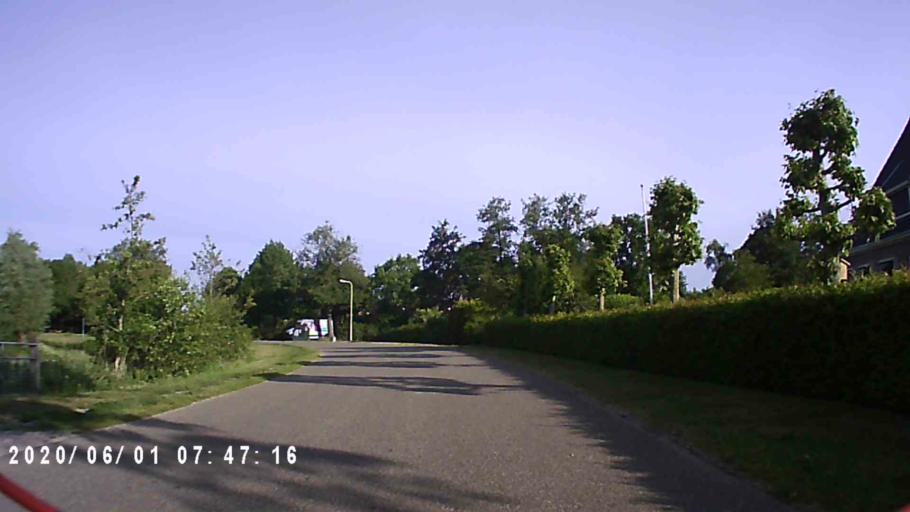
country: NL
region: Friesland
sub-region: Gemeente Dantumadiel
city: Rinsumageast
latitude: 53.2955
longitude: 5.9532
